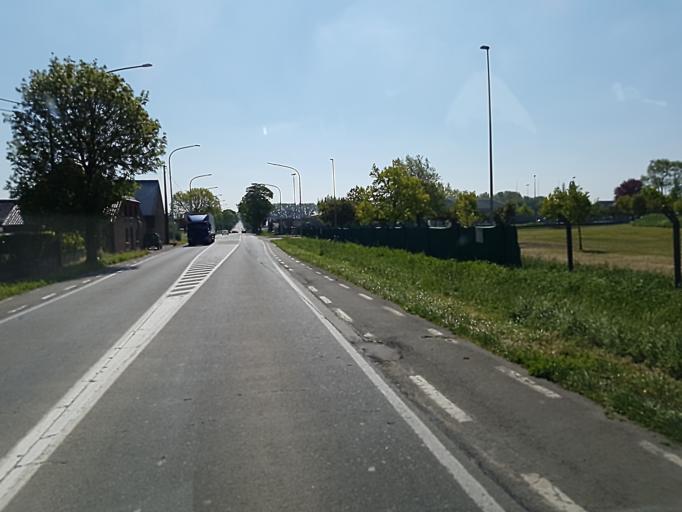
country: BE
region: Wallonia
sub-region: Province du Hainaut
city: Brugelette
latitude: 50.5879
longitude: 3.8437
